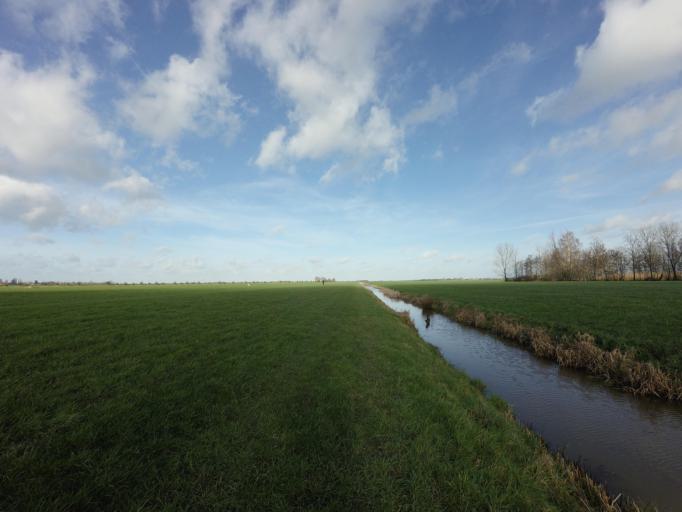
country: NL
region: Utrecht
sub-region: Gemeente Woerden
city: Woerden
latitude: 52.0943
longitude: 4.8716
